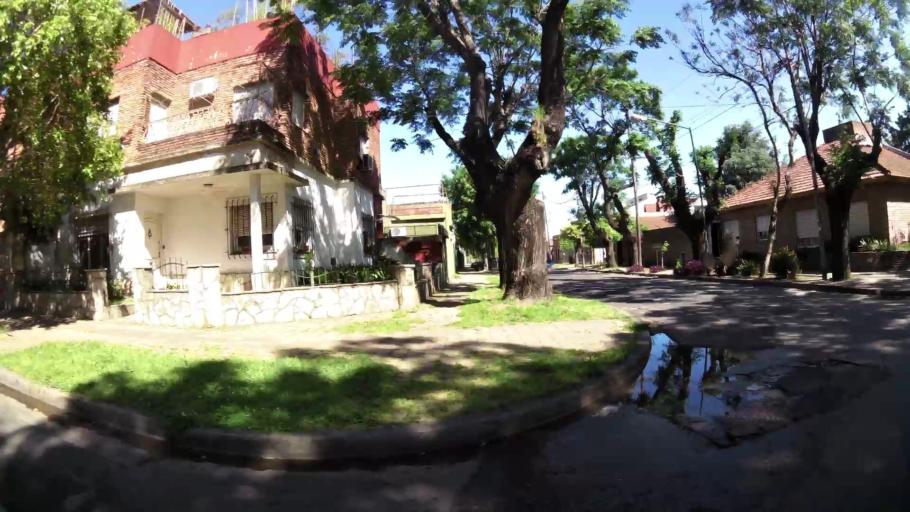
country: AR
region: Buenos Aires
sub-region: Partido de San Isidro
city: San Isidro
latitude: -34.5093
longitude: -58.5728
